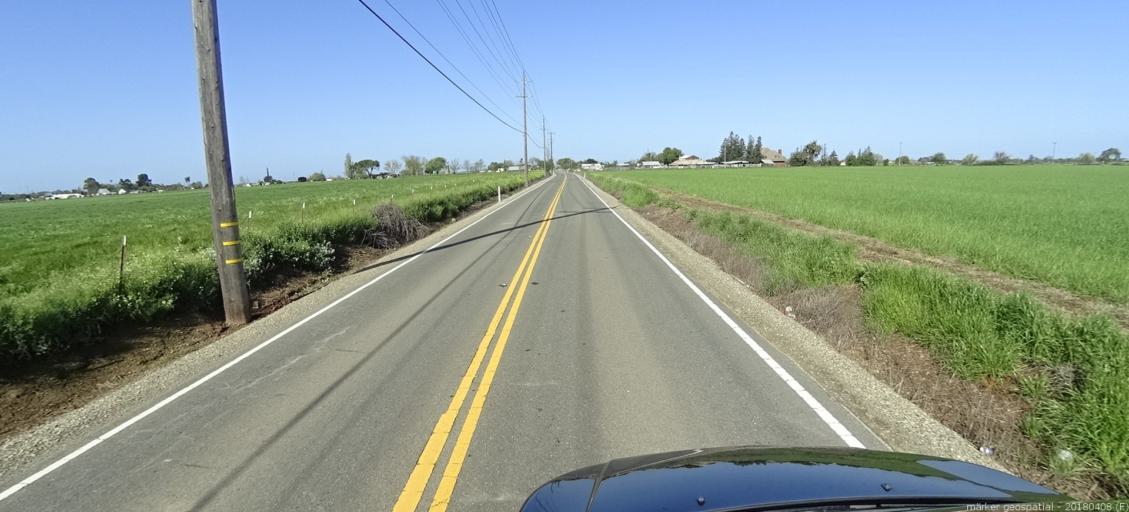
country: US
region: California
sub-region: Sacramento County
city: Elk Grove
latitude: 38.3726
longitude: -121.3964
